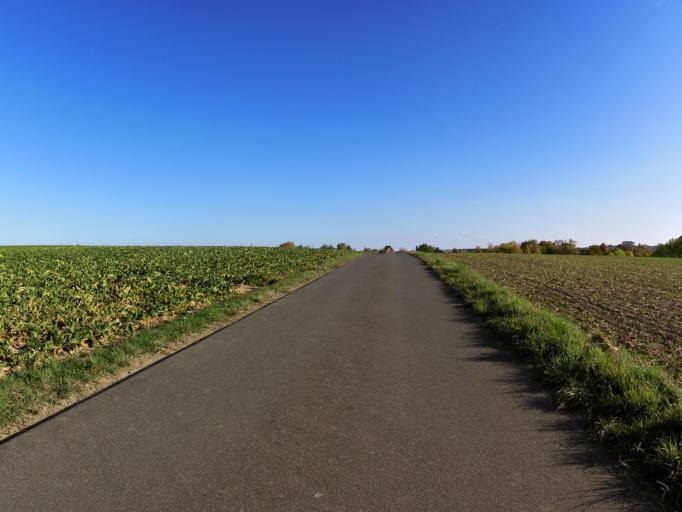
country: DE
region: Bavaria
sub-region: Regierungsbezirk Unterfranken
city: Reichenberg
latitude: 49.7156
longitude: 9.9264
